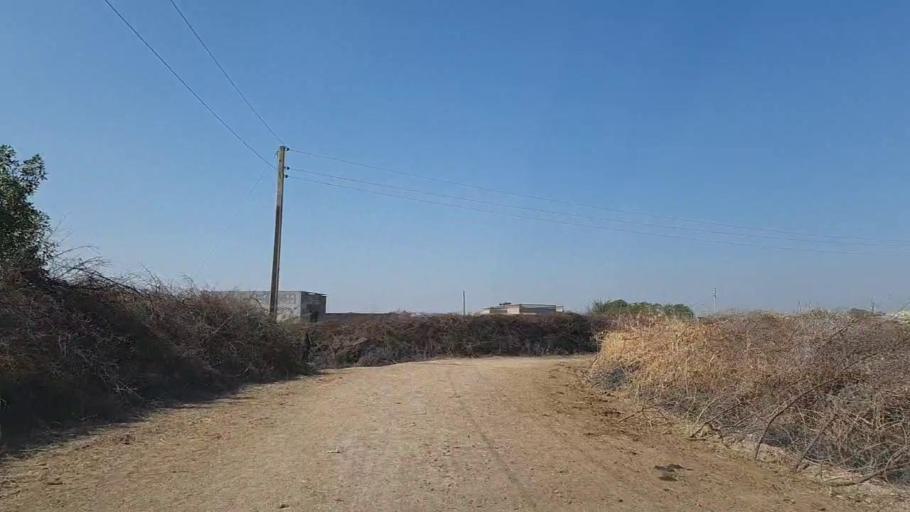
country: PK
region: Sindh
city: Pithoro
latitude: 25.4315
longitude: 69.3741
